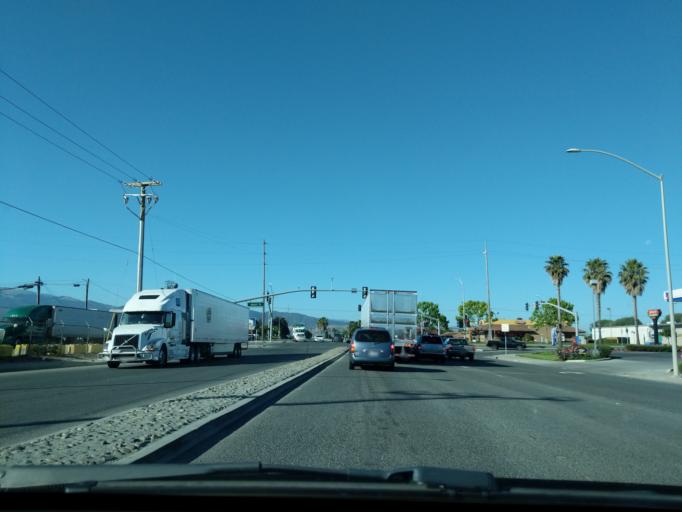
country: US
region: California
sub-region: Monterey County
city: Salinas
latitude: 36.6580
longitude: -121.6354
